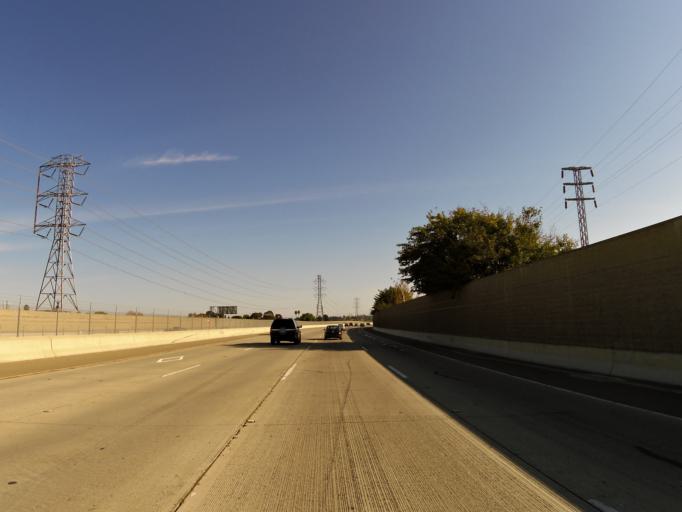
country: US
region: California
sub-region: Contra Costa County
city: Pittsburg
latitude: 38.0197
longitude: -121.9224
